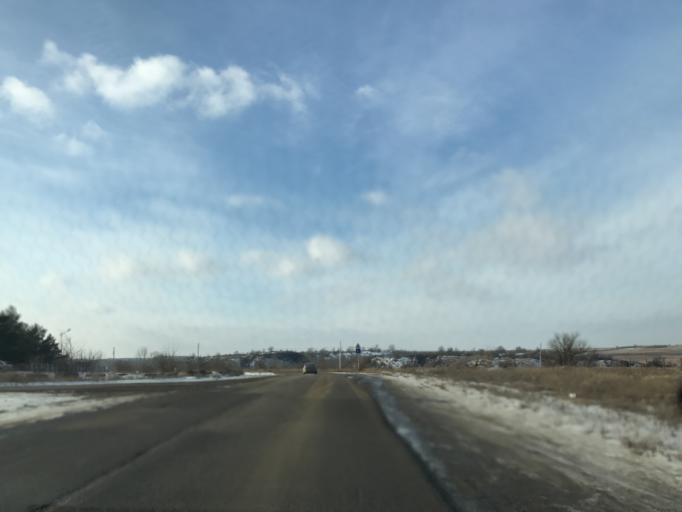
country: RU
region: Rostov
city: Staraya Stanitsa
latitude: 48.2409
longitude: 40.4108
